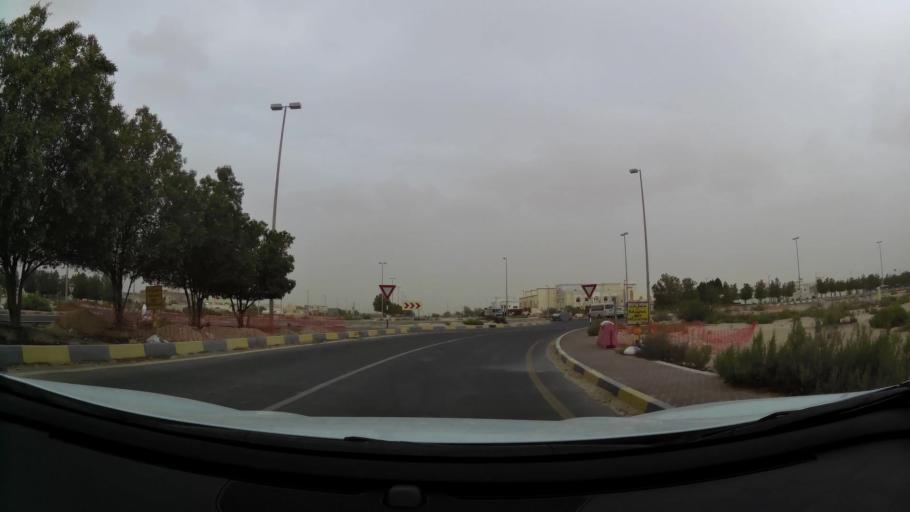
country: AE
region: Abu Dhabi
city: Abu Dhabi
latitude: 24.3849
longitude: 54.6957
